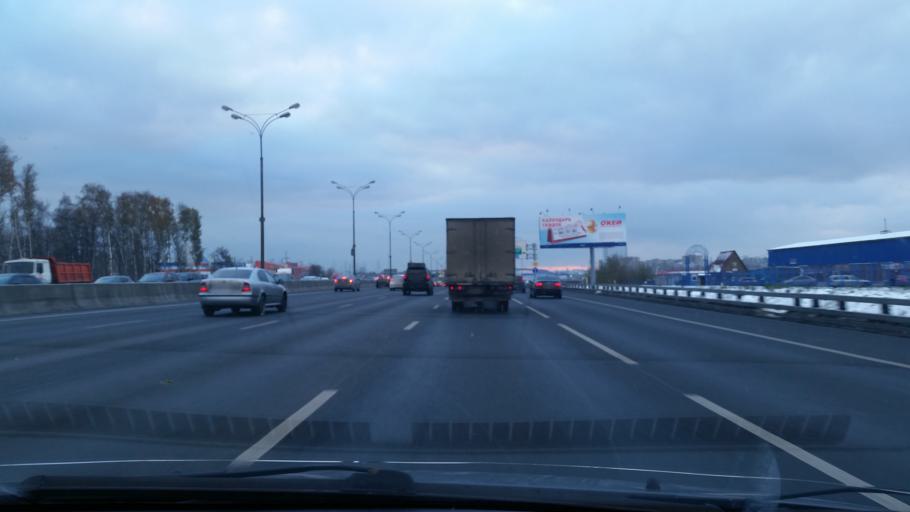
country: RU
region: Moscow
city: Businovo
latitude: 55.8961
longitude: 37.5051
